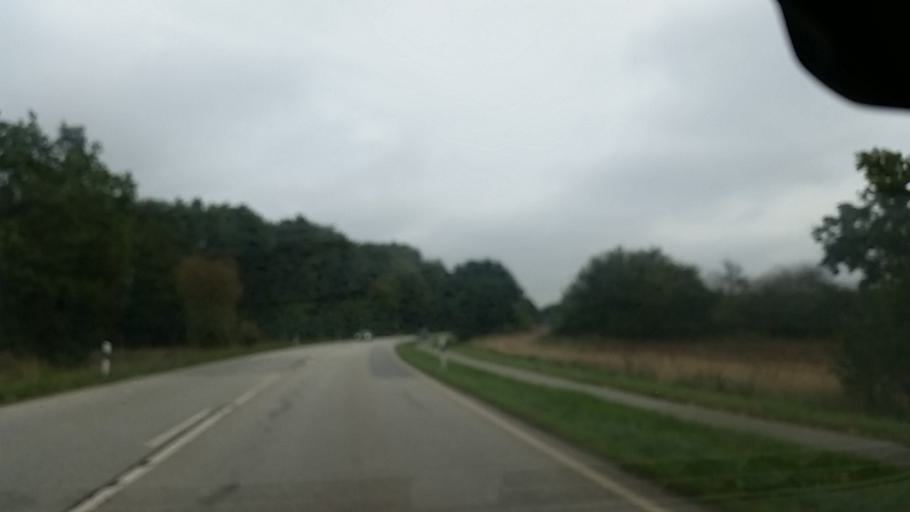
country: DE
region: Schleswig-Holstein
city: Hogersdorf
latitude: 53.9328
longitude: 10.2694
